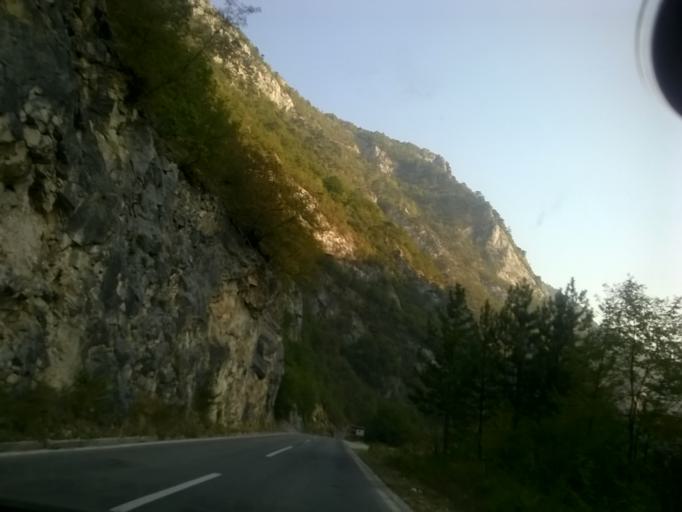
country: ME
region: Opstina Pluzine
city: Pluzine
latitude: 43.2117
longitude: 18.8586
